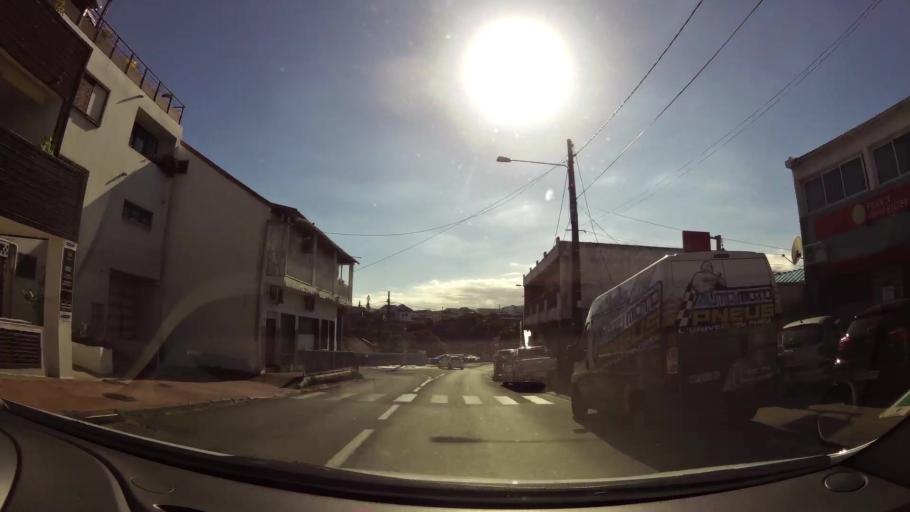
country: RE
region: Reunion
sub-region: Reunion
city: Saint-Pierre
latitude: -21.3426
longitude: 55.4805
